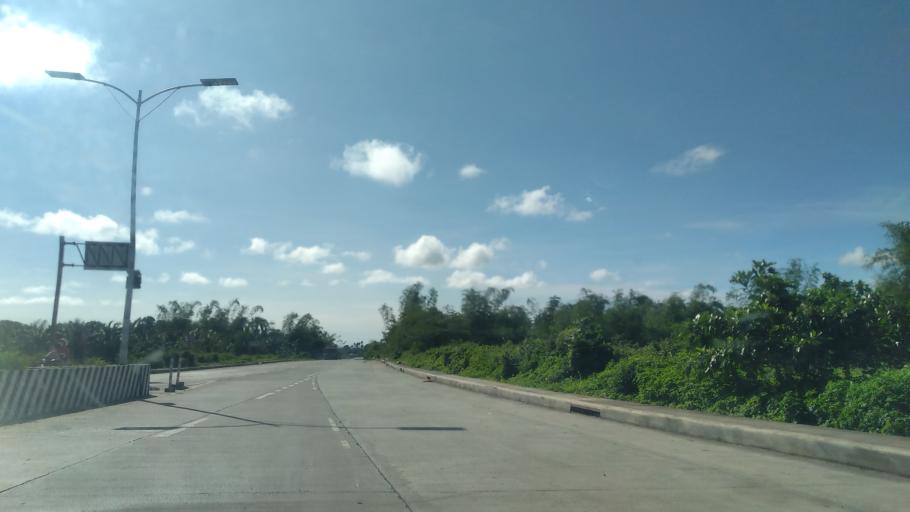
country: PH
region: Calabarzon
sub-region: Province of Quezon
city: Isabang
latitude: 13.9612
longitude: 121.5774
